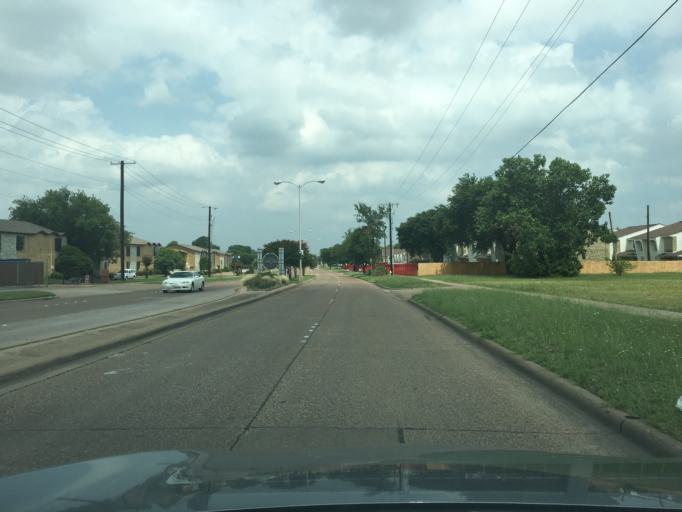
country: US
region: Texas
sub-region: Dallas County
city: Richardson
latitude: 32.9165
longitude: -96.6988
